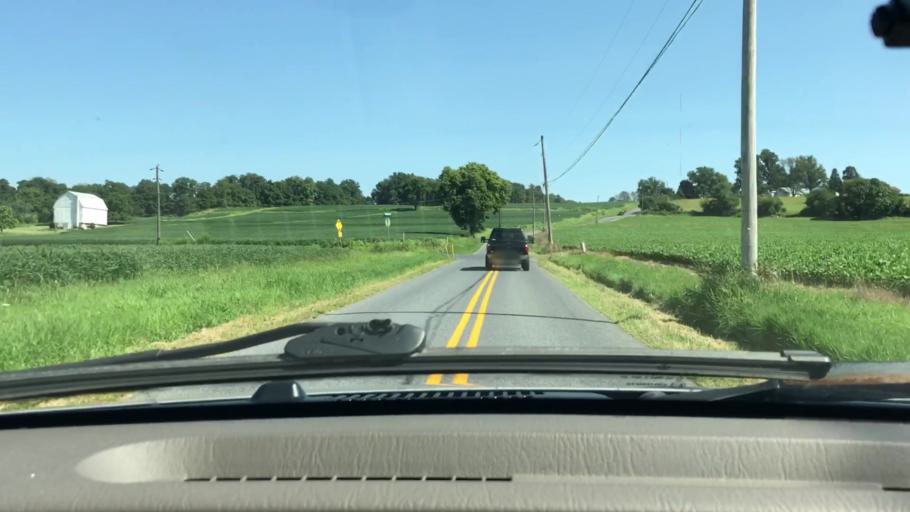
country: US
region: Pennsylvania
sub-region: Lancaster County
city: Elizabethtown
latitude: 40.1815
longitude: -76.6097
